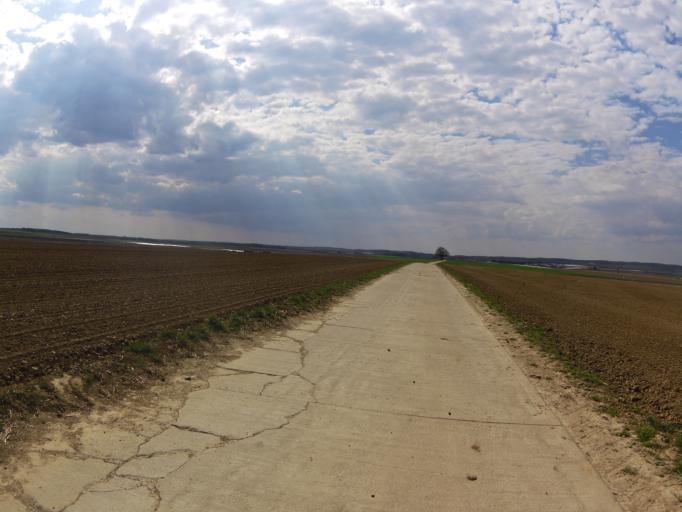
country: DE
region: Bavaria
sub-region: Regierungsbezirk Unterfranken
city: Oberpleichfeld
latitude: 49.8700
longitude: 10.0889
